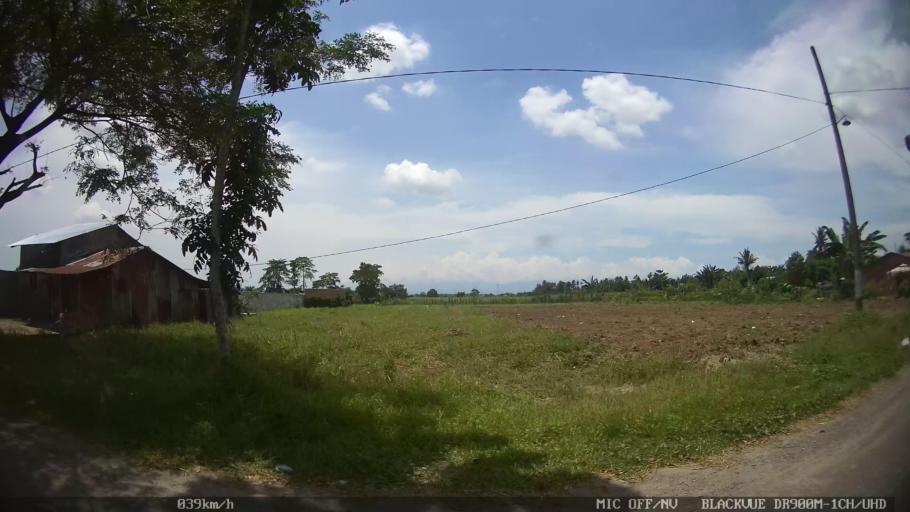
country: ID
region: North Sumatra
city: Binjai
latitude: 3.5912
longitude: 98.5202
